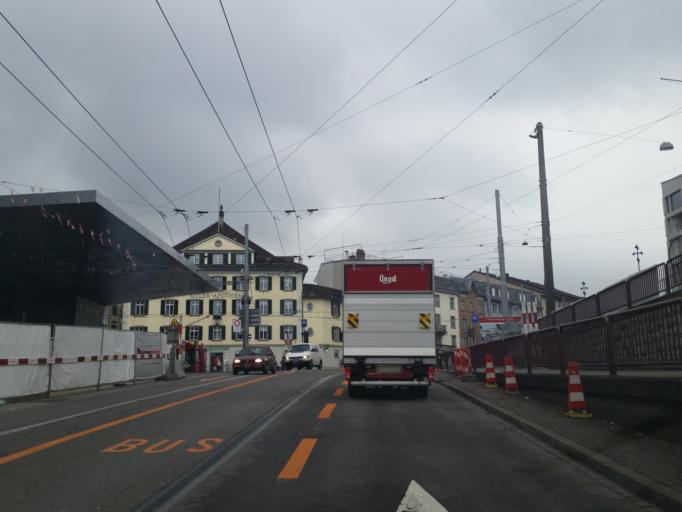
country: CH
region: Zurich
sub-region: Bezirk Winterthur
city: Winterthur
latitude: 47.4988
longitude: 8.7231
